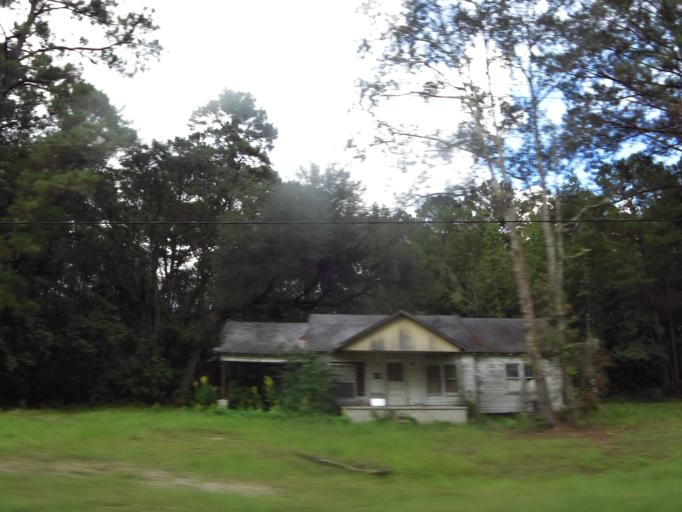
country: US
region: Georgia
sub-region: Liberty County
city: Midway
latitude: 31.8540
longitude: -81.4247
